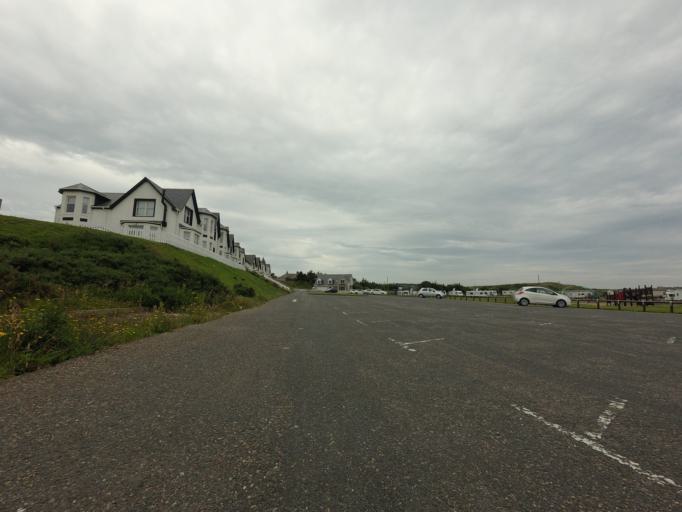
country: GB
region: Scotland
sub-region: Aberdeenshire
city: Banff
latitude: 57.6695
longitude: -2.5518
